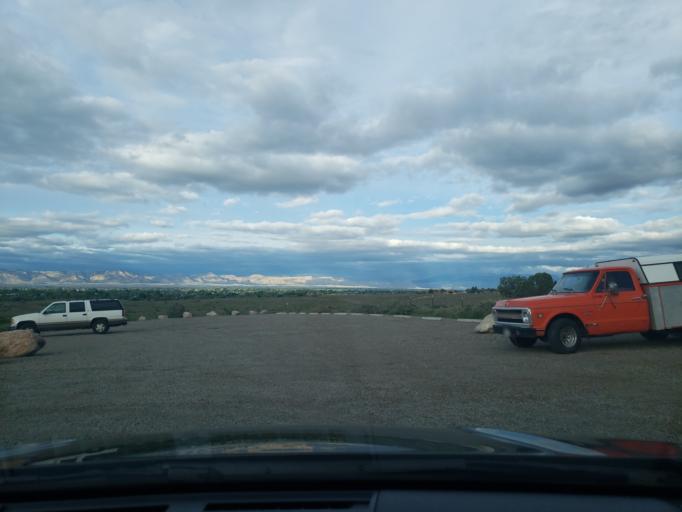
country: US
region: Colorado
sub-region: Mesa County
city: Fruita
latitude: 39.1399
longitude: -108.7561
